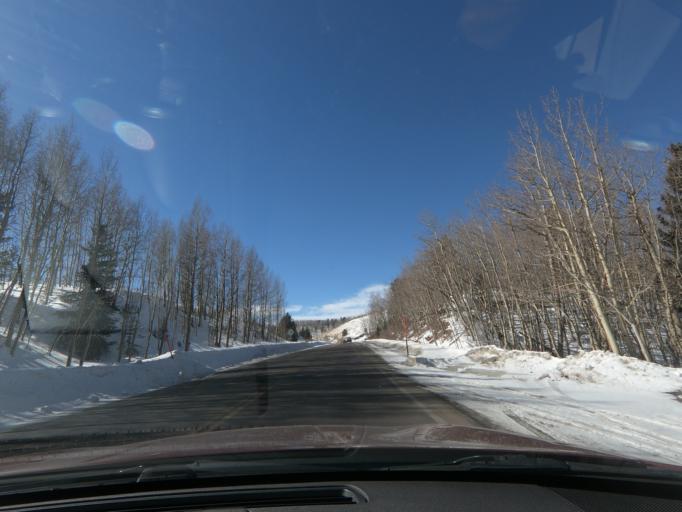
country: US
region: Colorado
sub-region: Teller County
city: Cripple Creek
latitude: 38.7994
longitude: -105.1192
